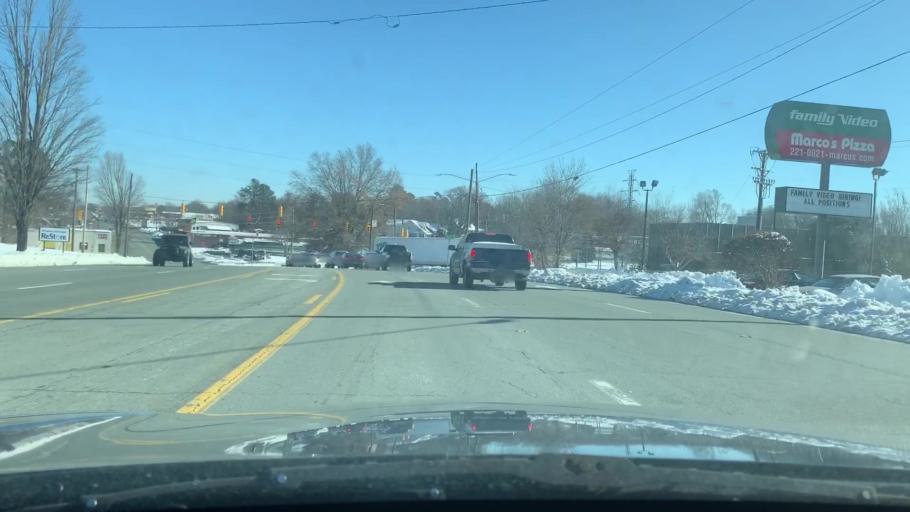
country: US
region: North Carolina
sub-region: Alamance County
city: Burlington
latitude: 36.0984
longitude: -79.4194
